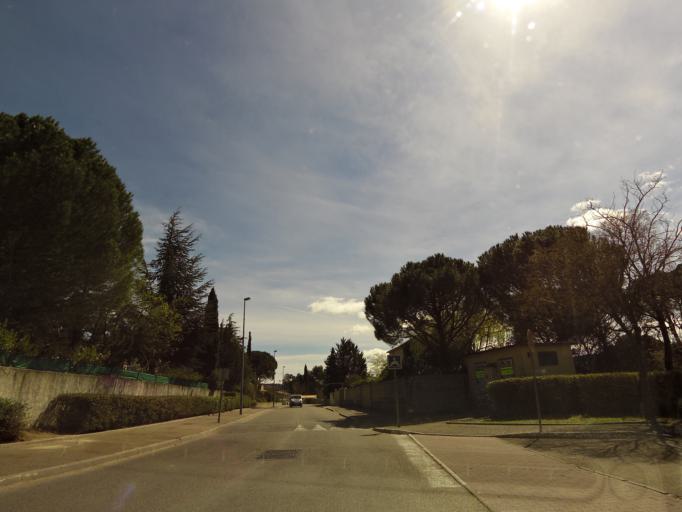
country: FR
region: Languedoc-Roussillon
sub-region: Departement du Gard
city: Clarensac
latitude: 43.8210
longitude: 4.2306
